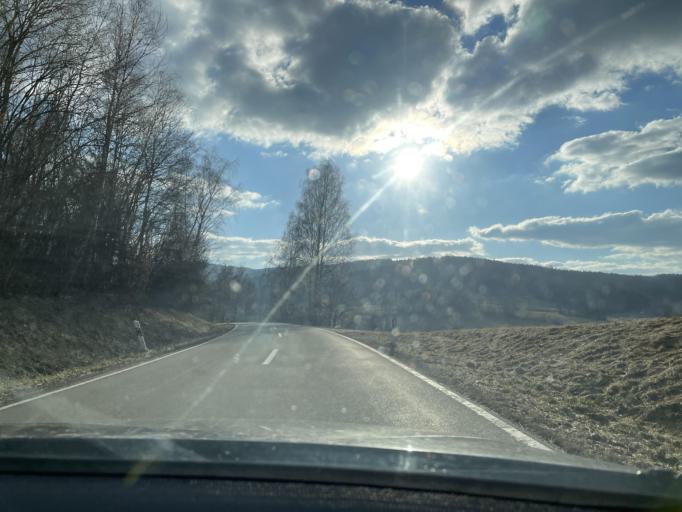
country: DE
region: Bavaria
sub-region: Lower Bavaria
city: Kollnburg
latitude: 49.0630
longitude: 12.8590
